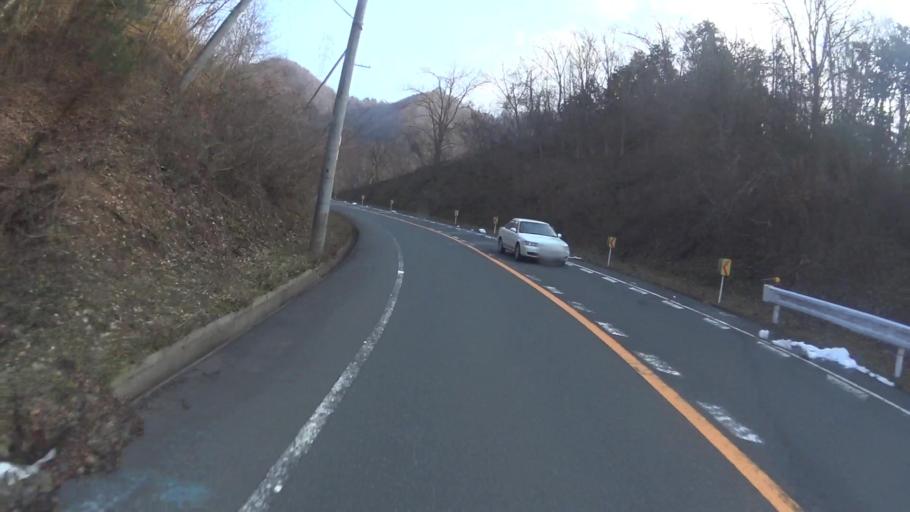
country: JP
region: Kyoto
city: Maizuru
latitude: 35.4325
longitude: 135.4015
